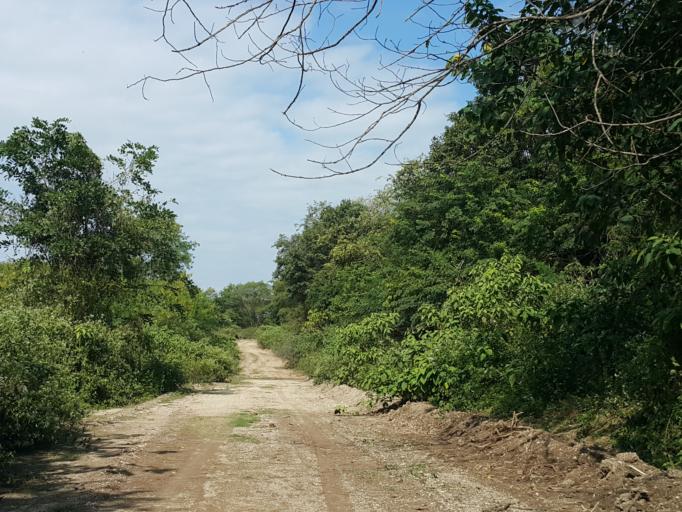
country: TH
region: Lampang
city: Mae Mo
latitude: 18.3299
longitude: 99.7656
